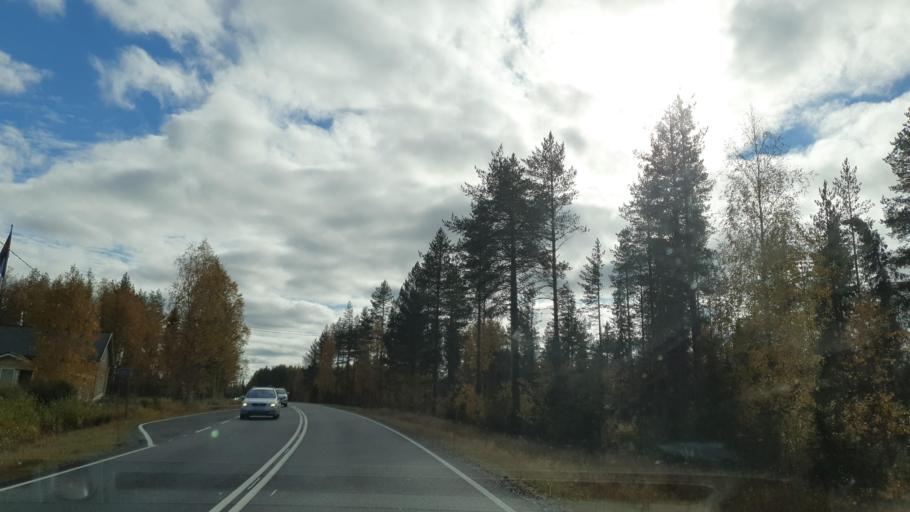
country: FI
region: Kainuu
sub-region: Kehys-Kainuu
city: Puolanka
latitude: 65.3266
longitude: 27.4453
